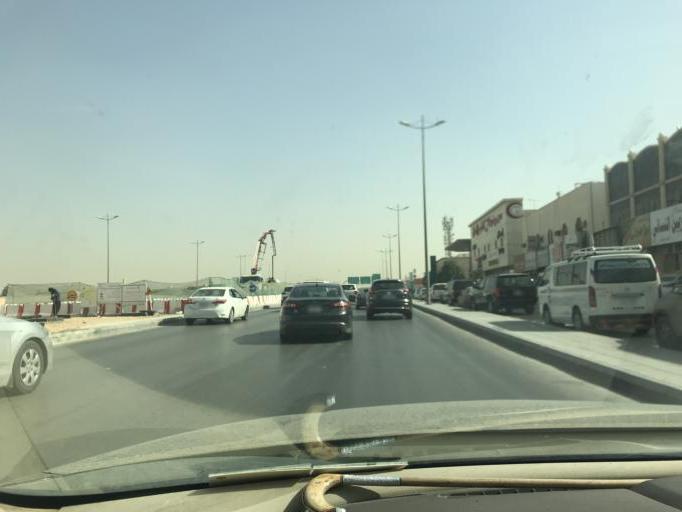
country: SA
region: Ar Riyad
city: Riyadh
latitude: 24.7909
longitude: 46.7448
